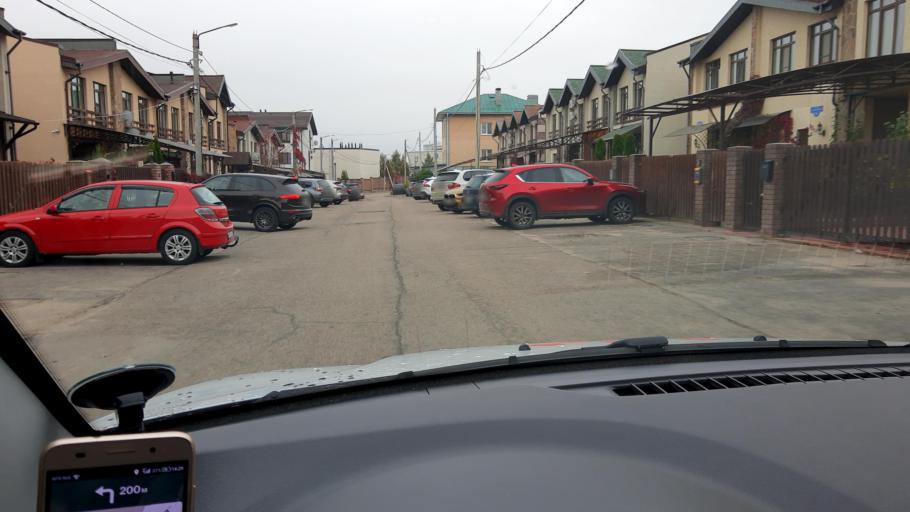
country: RU
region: Nizjnij Novgorod
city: Afonino
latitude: 56.2830
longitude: 44.0740
